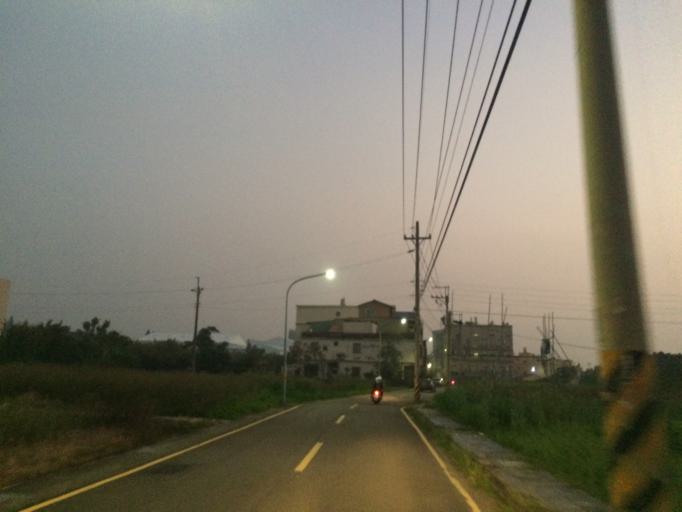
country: TW
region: Taiwan
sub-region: Hsinchu
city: Hsinchu
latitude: 24.7715
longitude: 120.9153
